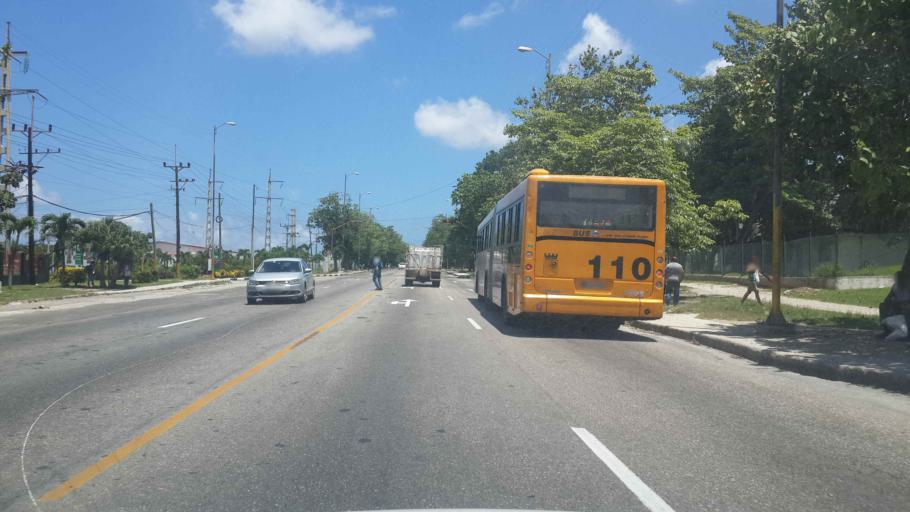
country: CU
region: La Habana
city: Guanabacoa
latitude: 23.1316
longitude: -82.3129
